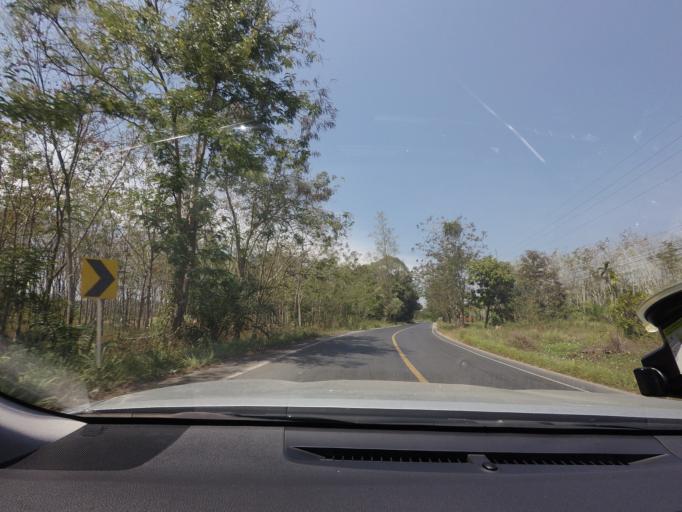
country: TH
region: Surat Thani
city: Tha Chang
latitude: 9.2617
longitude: 99.1736
